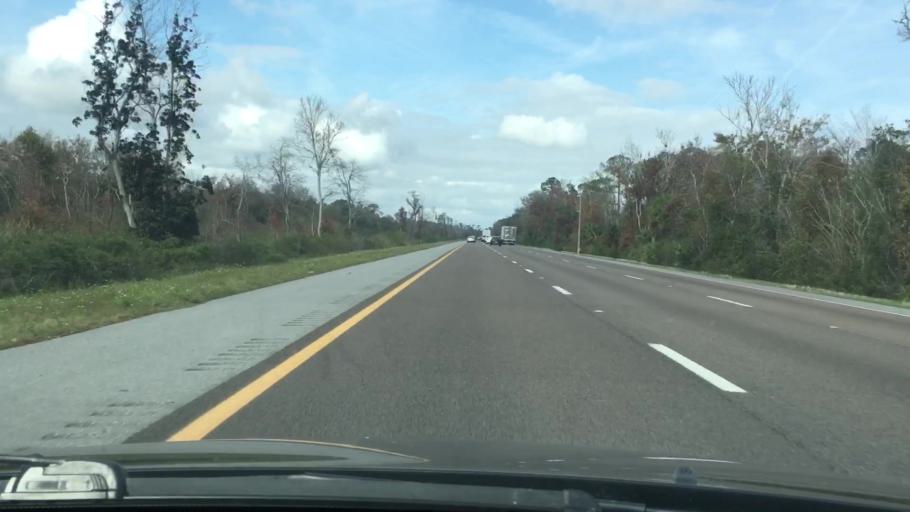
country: US
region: Florida
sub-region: Volusia County
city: Oak Hill
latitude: 28.8940
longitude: -80.9284
